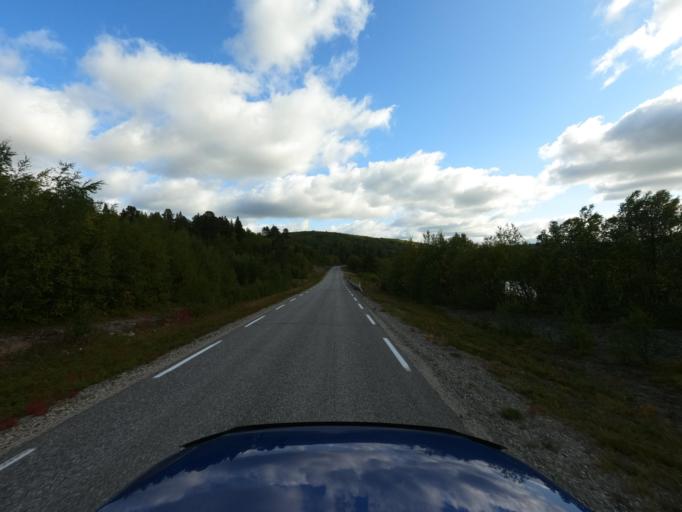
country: NO
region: Finnmark Fylke
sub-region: Karasjok
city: Karasjohka
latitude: 69.4301
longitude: 24.8908
